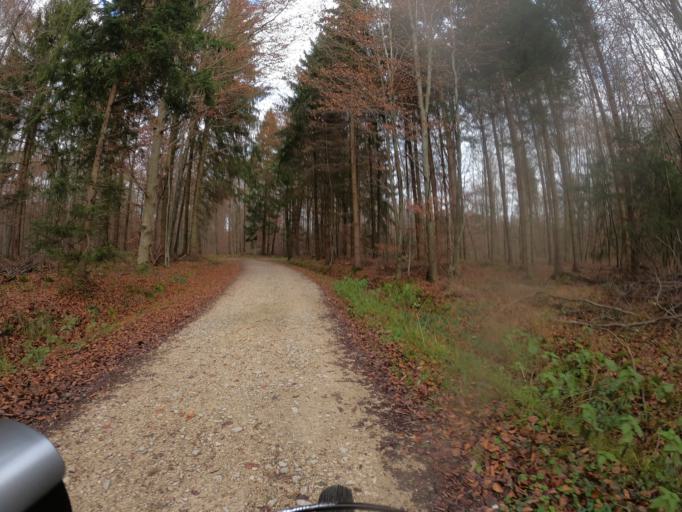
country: DE
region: Baden-Wuerttemberg
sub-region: Regierungsbezirk Stuttgart
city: Notzingen
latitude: 48.6847
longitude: 9.4477
